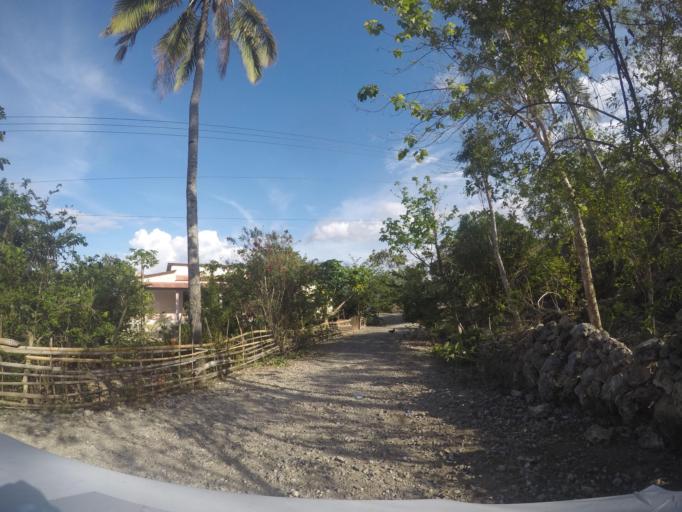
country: TL
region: Baucau
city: Baucau
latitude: -8.4700
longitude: 126.4650
